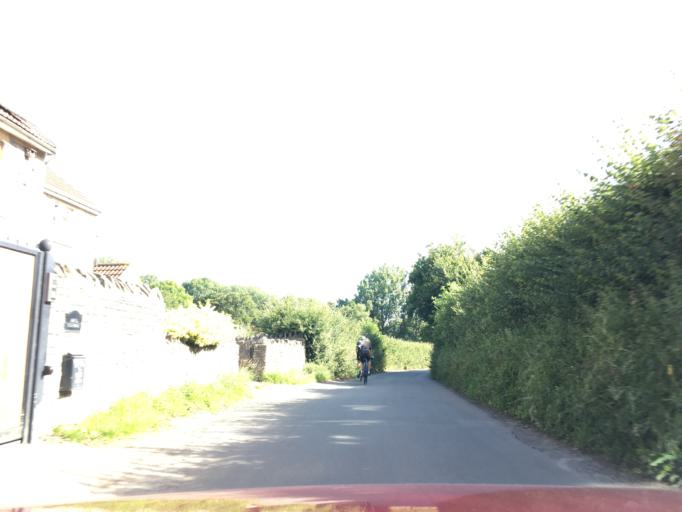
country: GB
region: England
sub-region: South Gloucestershire
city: Bitton
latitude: 51.4322
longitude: -2.4528
